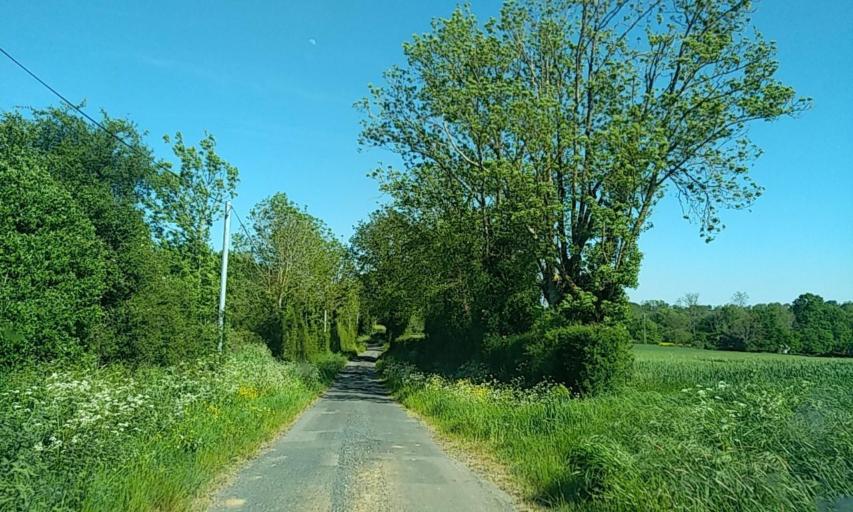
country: FR
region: Poitou-Charentes
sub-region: Departement des Deux-Sevres
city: Boisme
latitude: 46.7746
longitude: -0.4283
